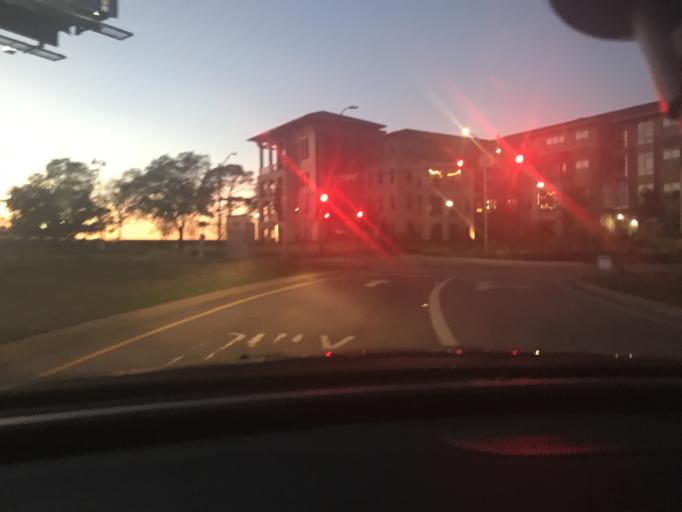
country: US
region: Texas
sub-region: Tarrant County
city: Arlington
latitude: 32.7603
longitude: -97.1102
